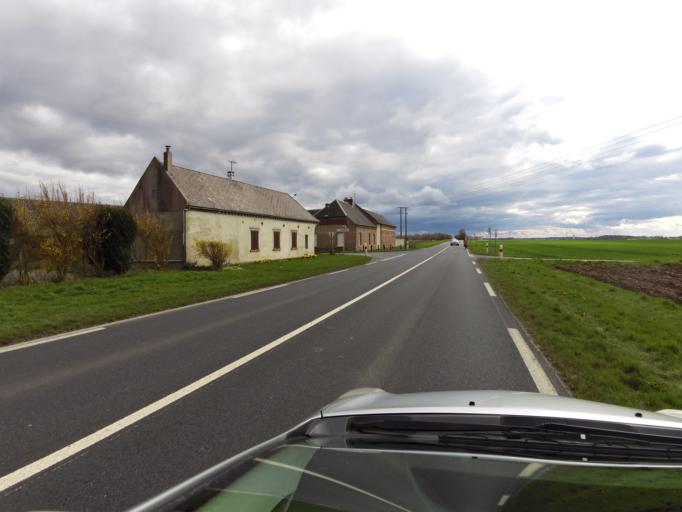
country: FR
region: Picardie
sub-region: Departement de la Somme
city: Roye
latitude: 49.7306
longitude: 2.8051
